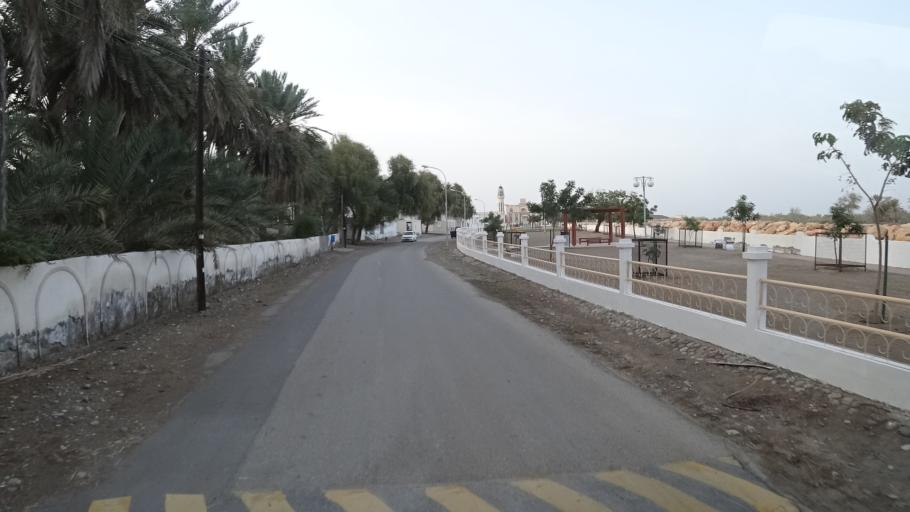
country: OM
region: Muhafazat Masqat
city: Muscat
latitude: 23.2137
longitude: 58.9738
